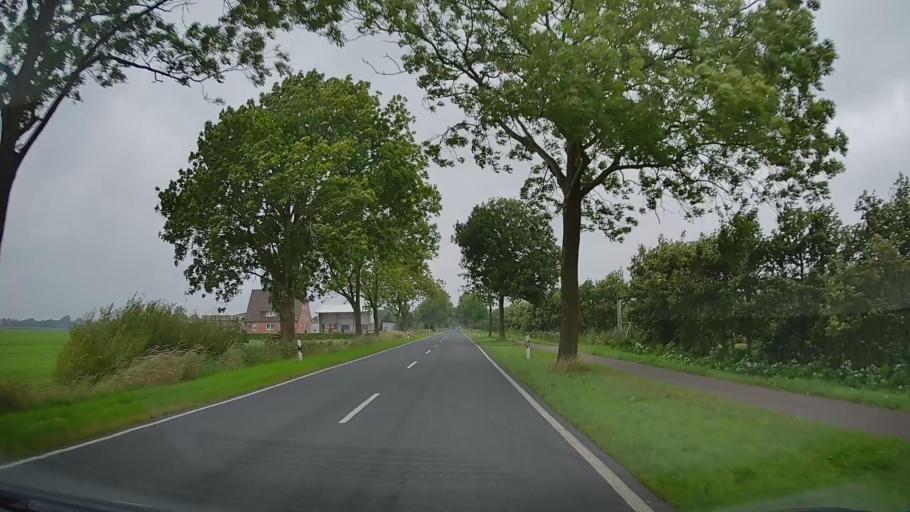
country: DE
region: Lower Saxony
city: Balje
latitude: 53.8167
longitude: 9.1310
